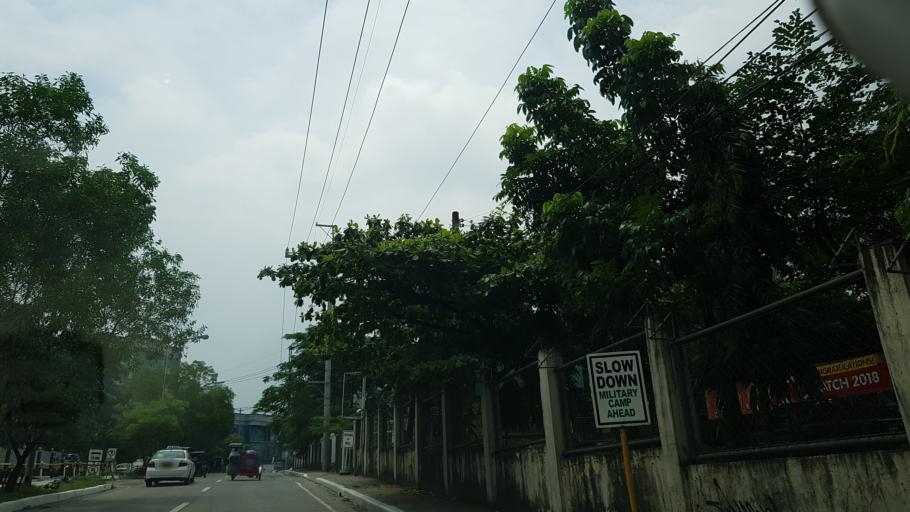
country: PH
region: Metro Manila
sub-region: Makati City
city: Makati City
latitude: 14.5249
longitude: 121.0449
